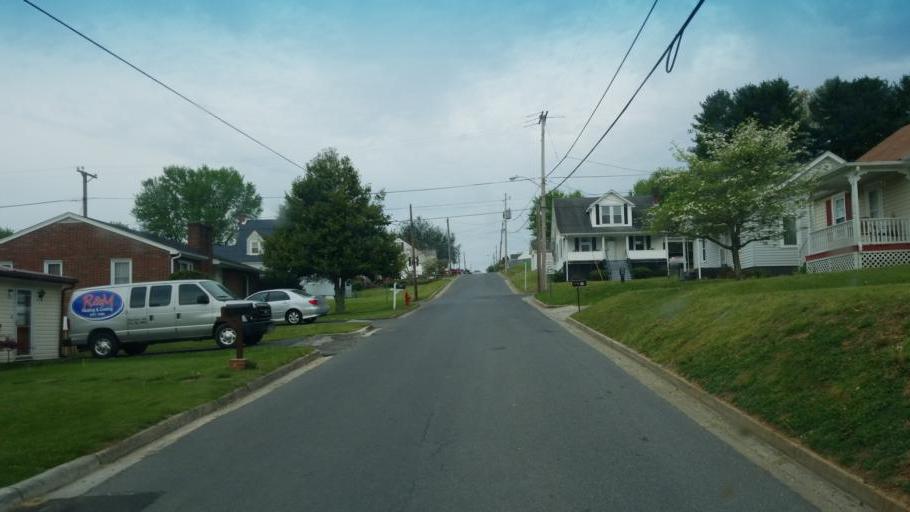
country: US
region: Virginia
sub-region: Smyth County
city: Marion
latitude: 36.8422
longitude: -81.5214
